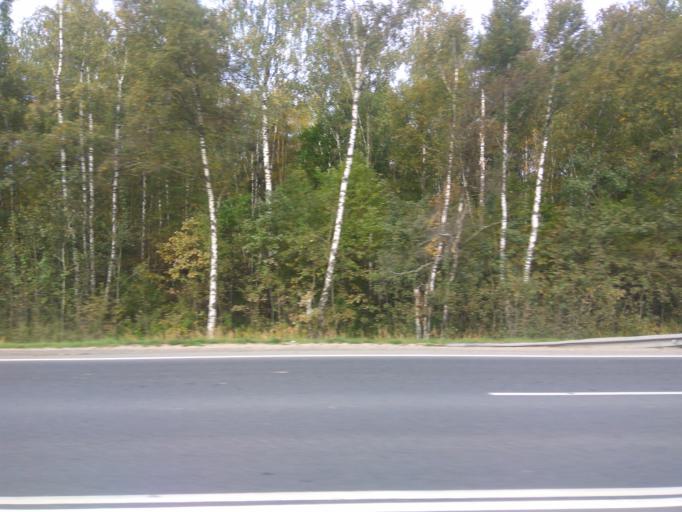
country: RU
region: Moskovskaya
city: Medvezh'i Ozera
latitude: 55.8748
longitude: 37.9971
